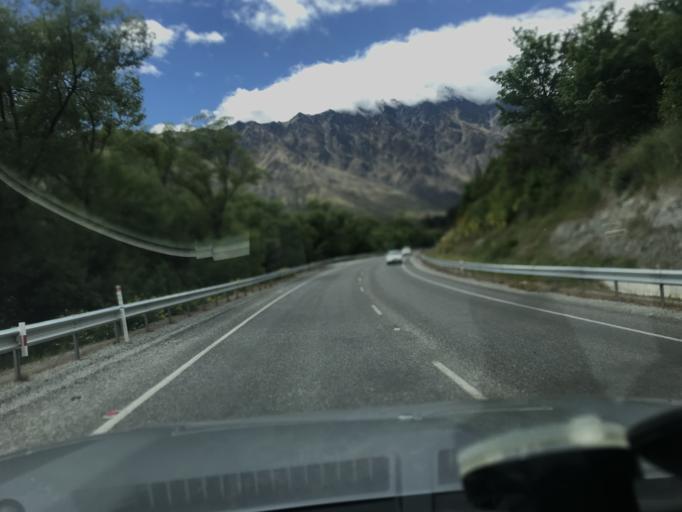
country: NZ
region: Otago
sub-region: Queenstown-Lakes District
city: Queenstown
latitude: -45.0307
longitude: 168.7362
